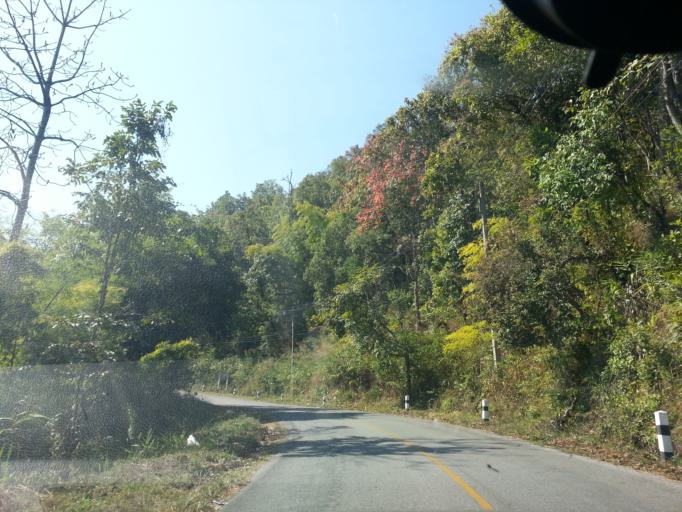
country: TH
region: Chiang Mai
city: Chai Prakan
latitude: 19.8359
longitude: 99.0948
